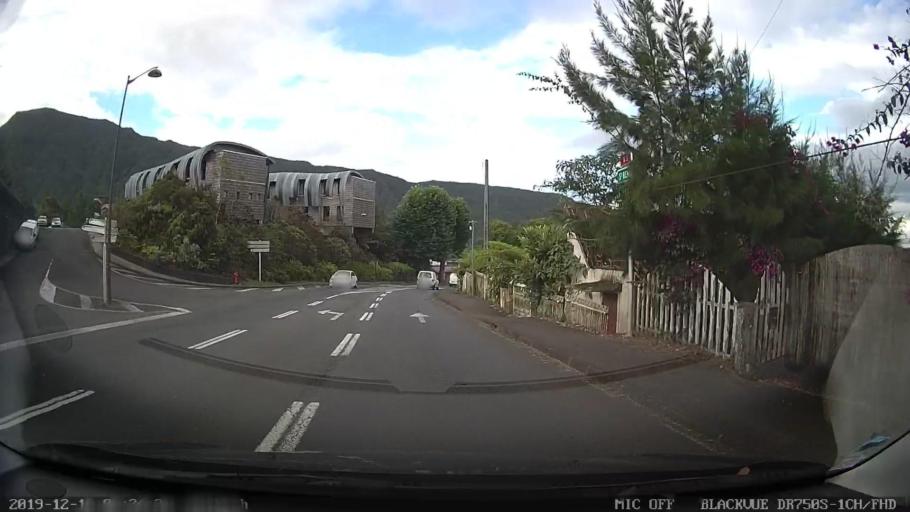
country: RE
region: Reunion
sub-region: Reunion
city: Saint-Benoit
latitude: -21.1372
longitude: 55.6245
